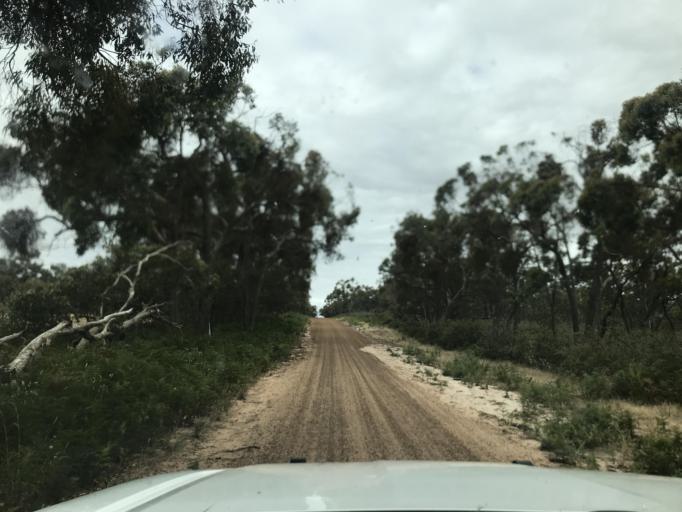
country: AU
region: South Australia
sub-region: Naracoorte and Lucindale
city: Naracoorte
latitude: -36.9218
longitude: 141.3228
